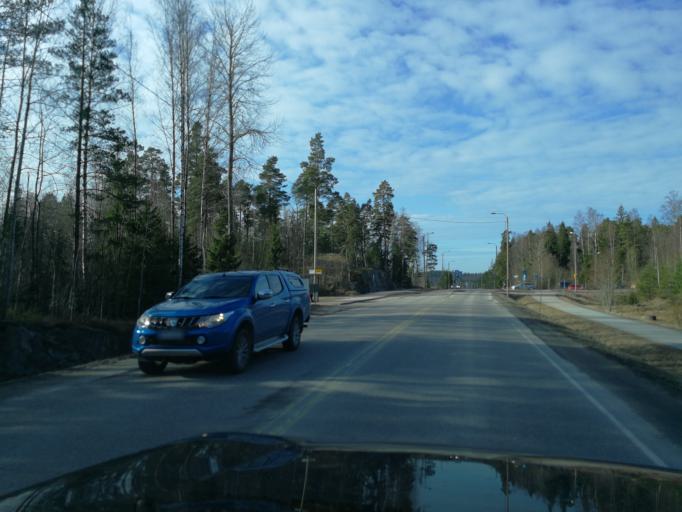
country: FI
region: Uusimaa
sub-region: Helsinki
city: Kirkkonummi
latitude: 60.1096
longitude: 24.4442
